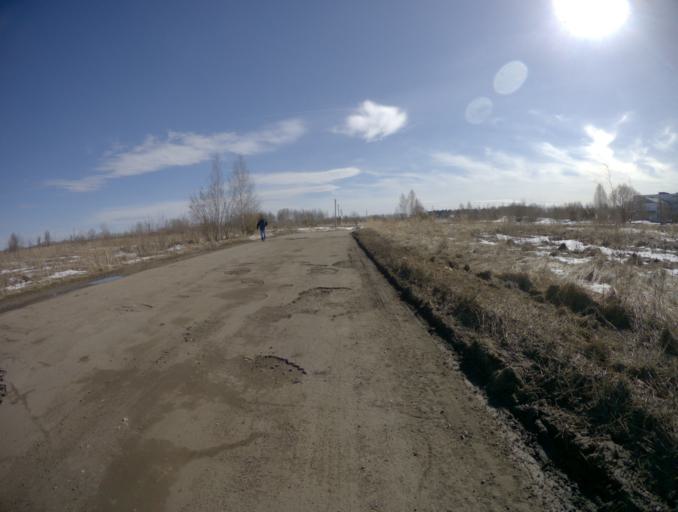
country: RU
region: Vladimir
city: Suzdal'
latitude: 56.4392
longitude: 40.4646
